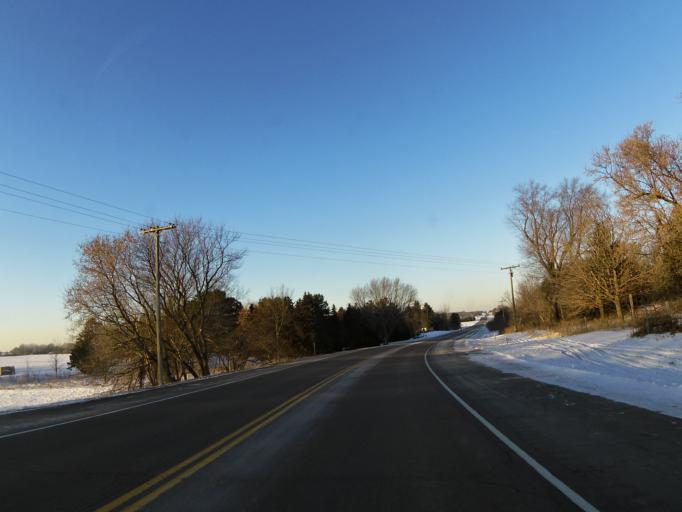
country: US
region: Minnesota
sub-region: Dakota County
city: Farmington
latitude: 44.5612
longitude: -93.1366
